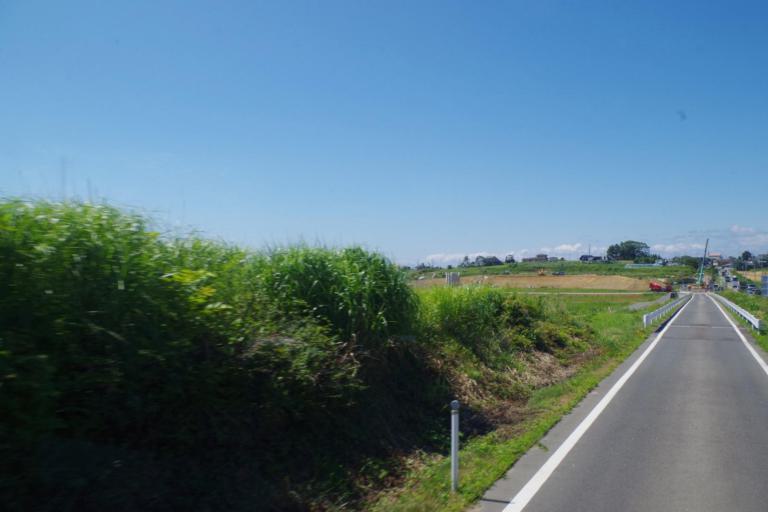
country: JP
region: Iwate
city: Ofunato
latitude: 38.8270
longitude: 141.5772
